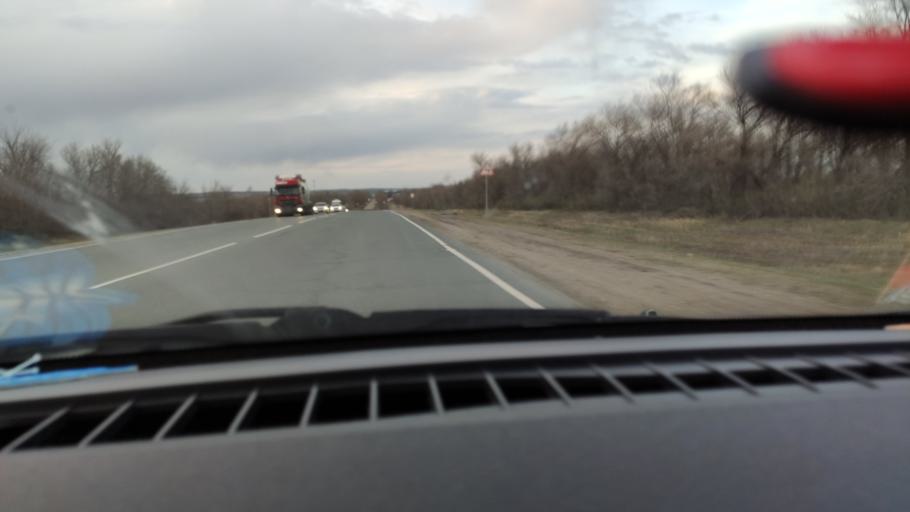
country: RU
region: Saratov
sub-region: Saratovskiy Rayon
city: Saratov
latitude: 51.7184
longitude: 46.0264
